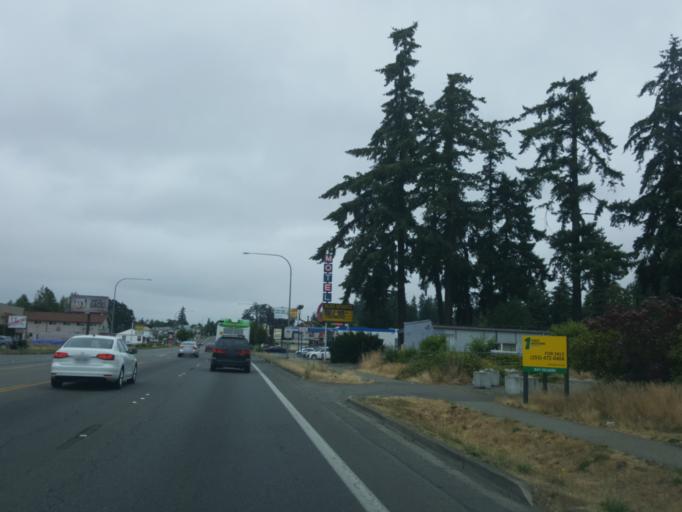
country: US
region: Washington
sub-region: Pierce County
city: Parkland
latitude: 47.1404
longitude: -122.4345
